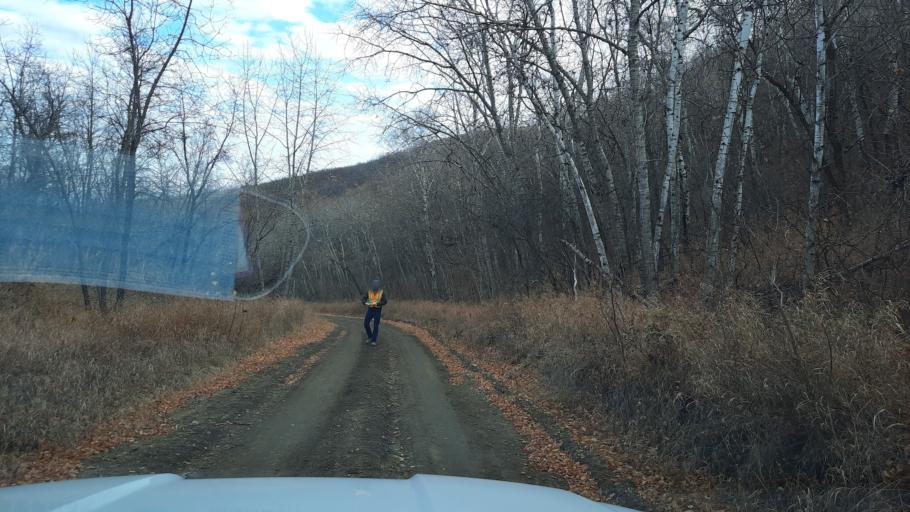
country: CA
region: Saskatchewan
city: Pilot Butte
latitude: 50.7759
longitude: -104.2124
